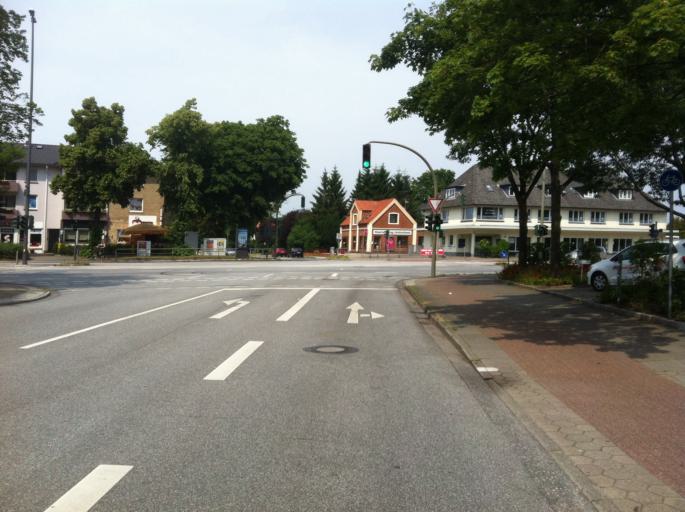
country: DE
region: Lower Saxony
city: Neu Wulmstorf
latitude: 53.4709
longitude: 9.8631
